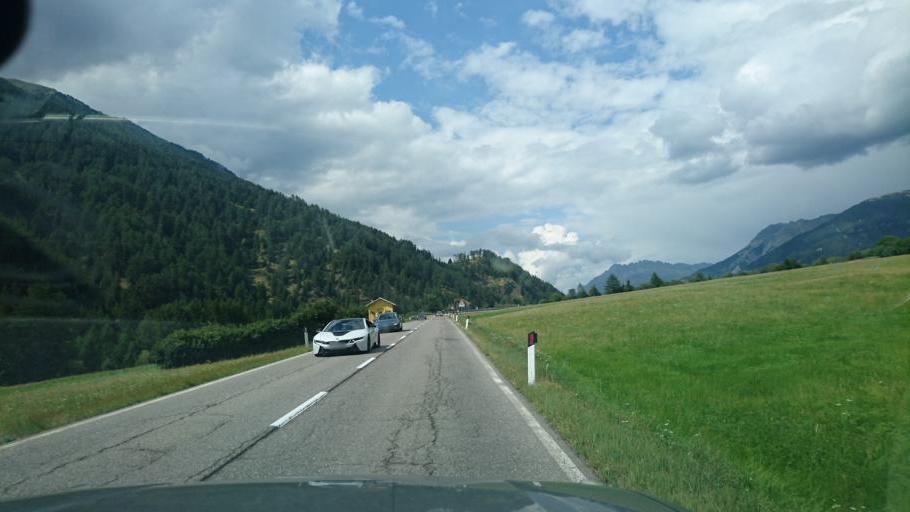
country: IT
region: Trentino-Alto Adige
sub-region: Bolzano
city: Malles Venosta
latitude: 46.7232
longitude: 10.5332
